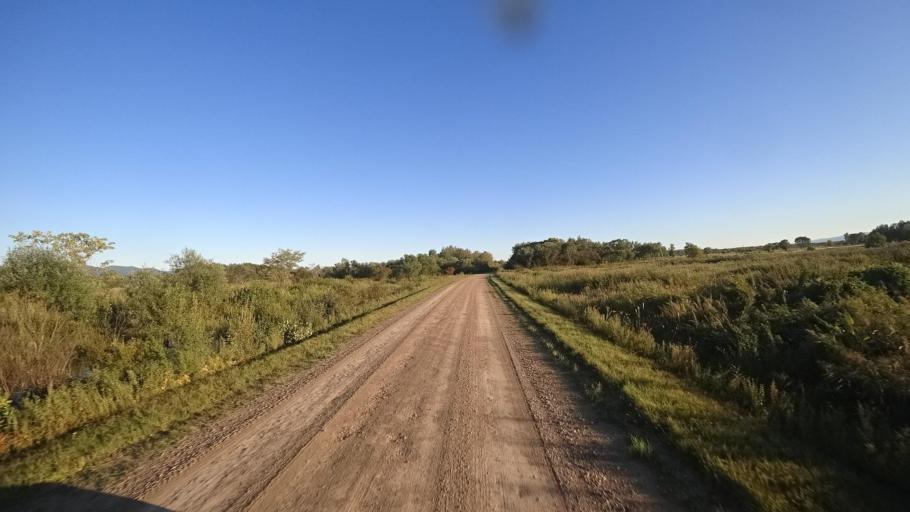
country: RU
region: Primorskiy
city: Kirovskiy
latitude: 44.7839
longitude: 133.6250
